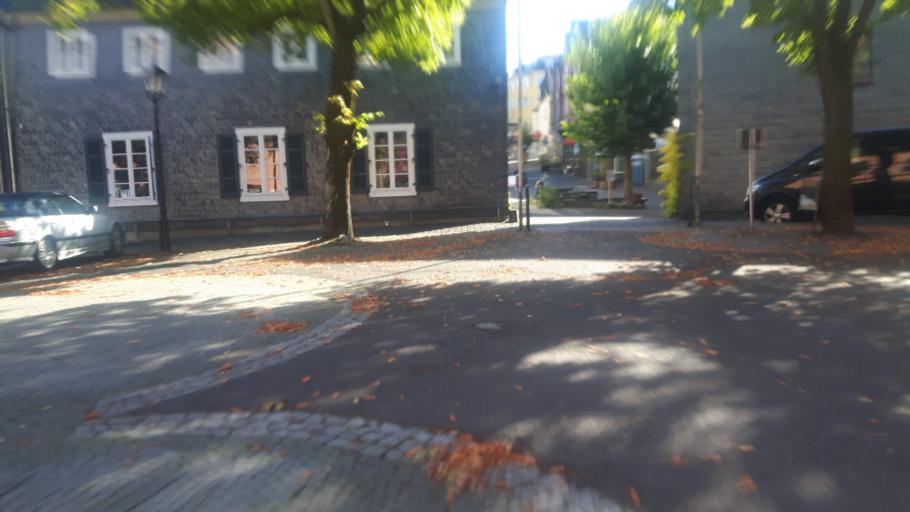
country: DE
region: Rheinland-Pfalz
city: Wissen
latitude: 50.7827
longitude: 7.7354
